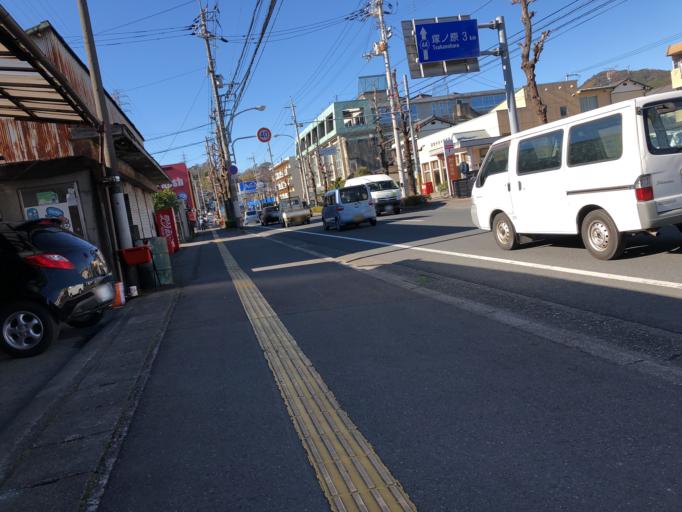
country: JP
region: Kochi
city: Kochi-shi
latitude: 33.5705
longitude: 133.5185
